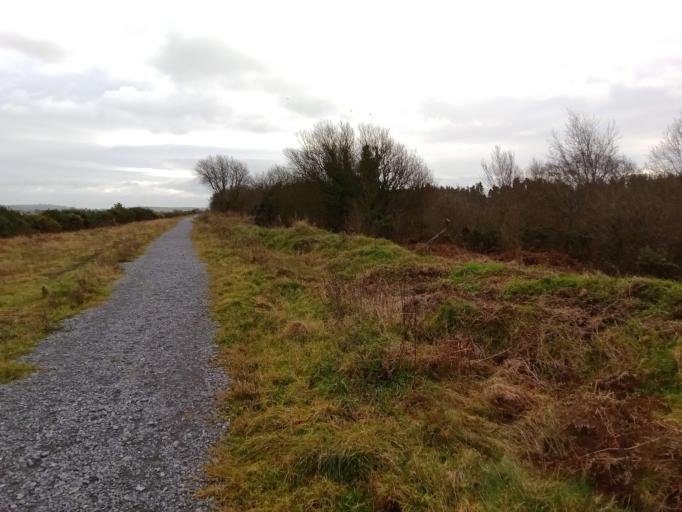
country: IE
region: Munster
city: Thurles
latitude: 52.5998
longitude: -7.7498
